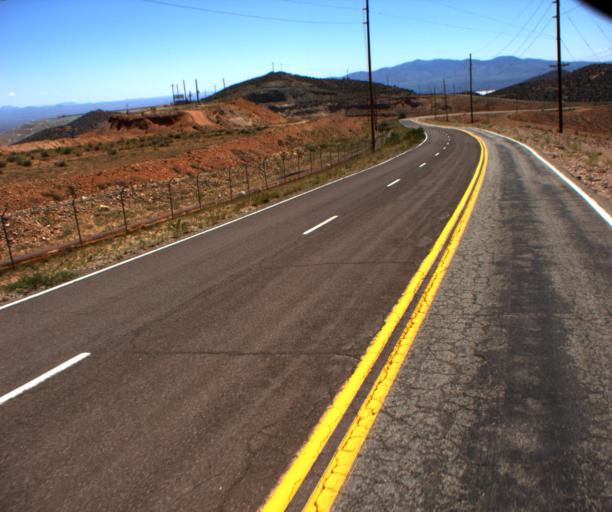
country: US
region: Arizona
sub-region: Greenlee County
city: Morenci
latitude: 33.0838
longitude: -109.3808
